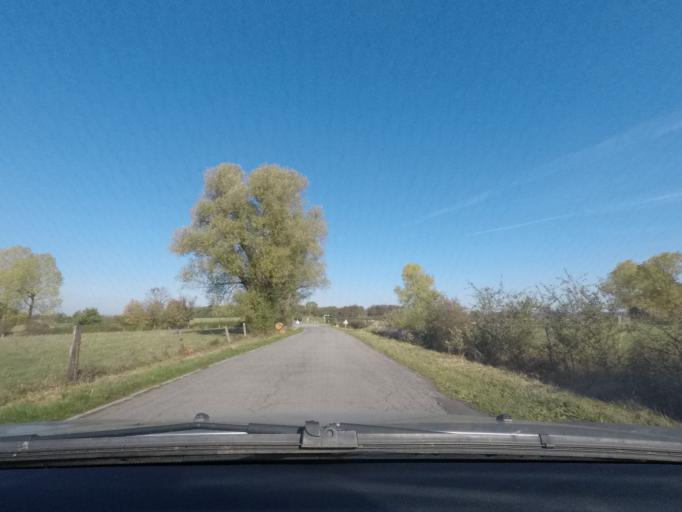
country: BE
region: Wallonia
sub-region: Province du Luxembourg
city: Etalle
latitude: 49.6995
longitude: 5.5701
